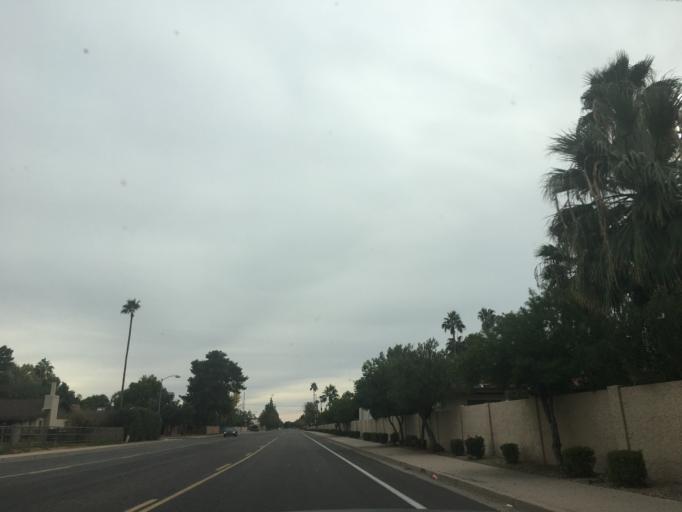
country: US
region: Arizona
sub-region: Maricopa County
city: Gilbert
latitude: 33.3639
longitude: -111.7821
